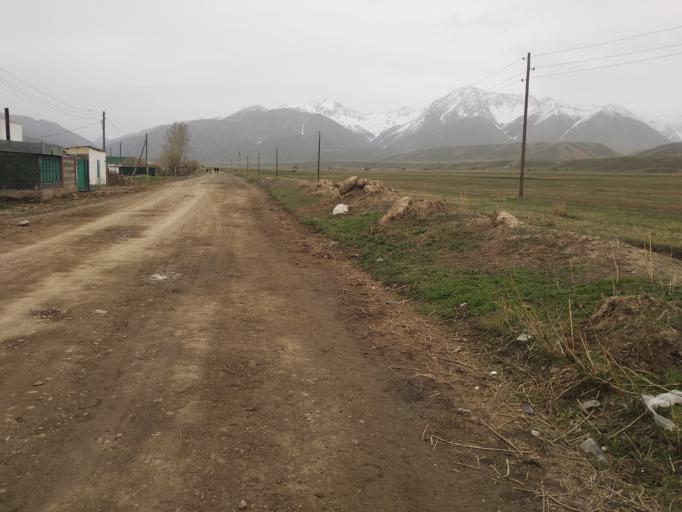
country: KG
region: Naryn
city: Naryn
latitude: 41.5161
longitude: 76.4403
